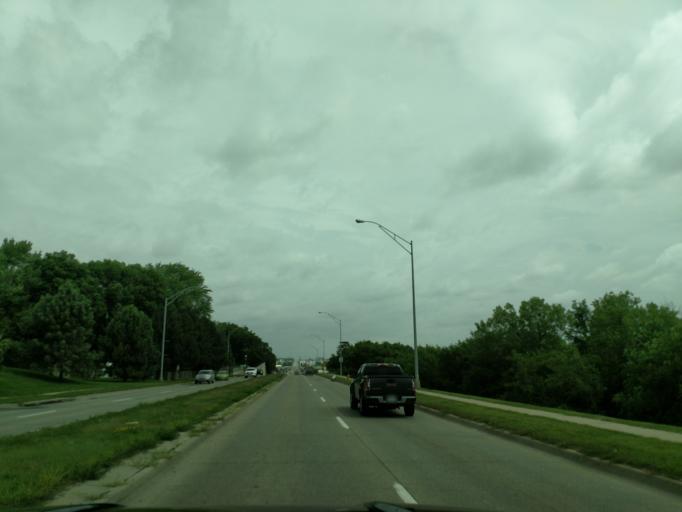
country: US
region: Nebraska
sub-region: Sarpy County
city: La Vista
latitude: 41.1953
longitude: -96.0238
